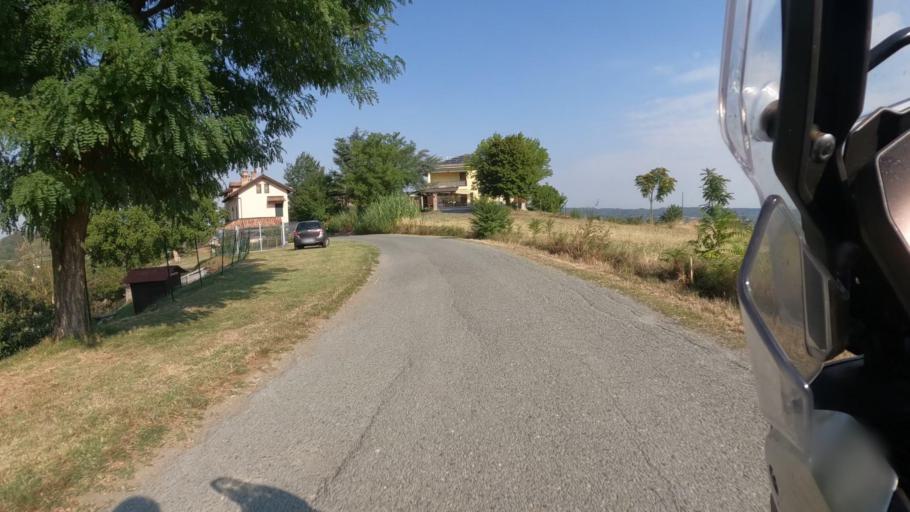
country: IT
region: Piedmont
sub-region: Provincia di Asti
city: Nizza Monferrato
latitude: 44.7600
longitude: 8.3799
